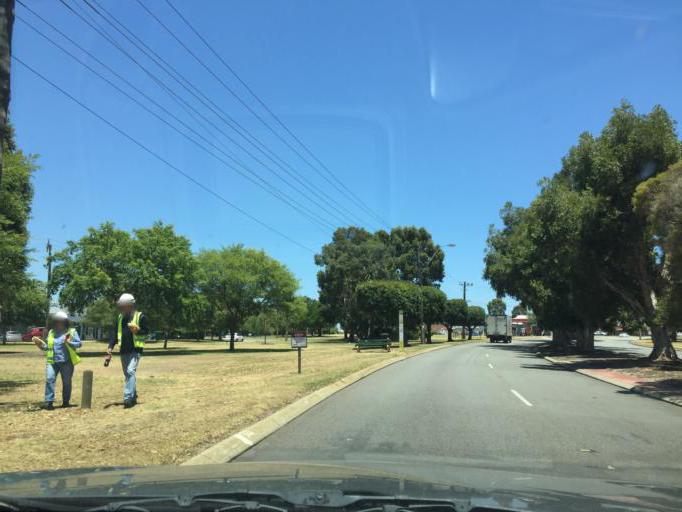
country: AU
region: Western Australia
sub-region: Canning
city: Canning Vale
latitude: -32.0624
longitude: 115.9281
